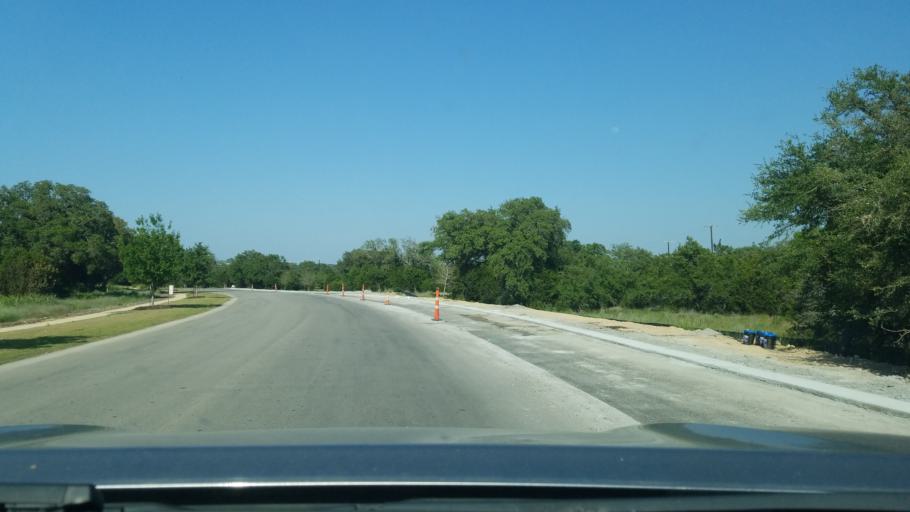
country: US
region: Texas
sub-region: Comal County
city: Bulverde
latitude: 29.7692
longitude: -98.4202
